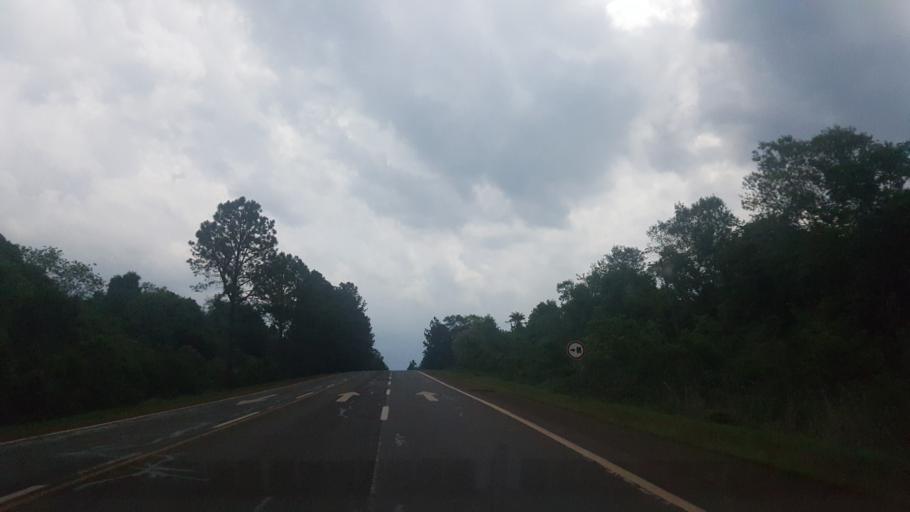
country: AR
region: Misiones
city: Santo Pipo
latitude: -27.1222
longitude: -55.3762
